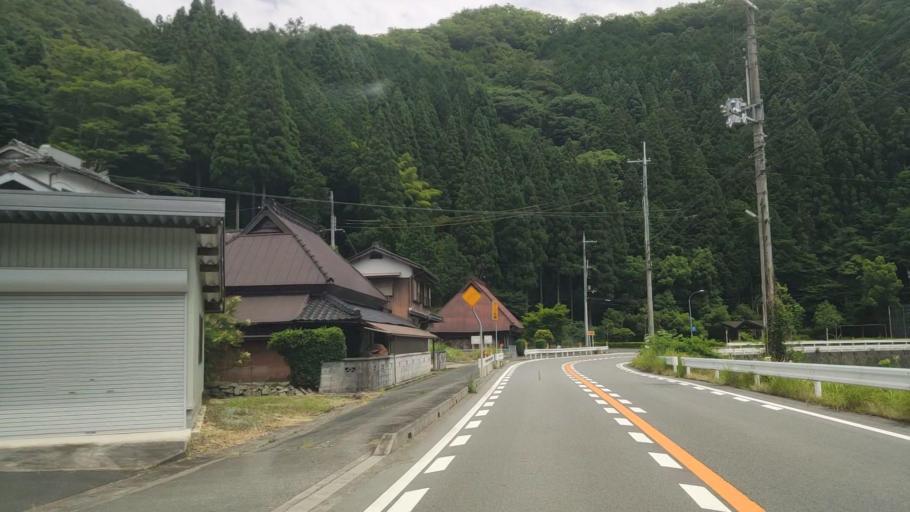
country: JP
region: Hyogo
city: Yamazakicho-nakabirose
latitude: 35.0714
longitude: 134.3600
